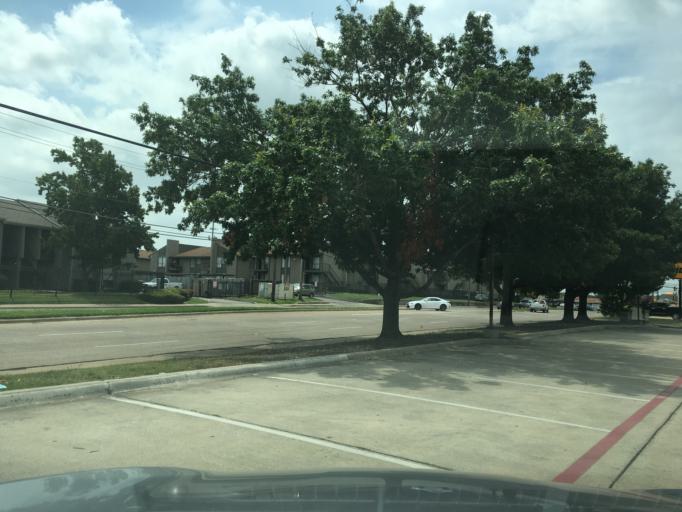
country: US
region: Texas
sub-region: Dallas County
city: Addison
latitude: 32.9344
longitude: -96.8137
